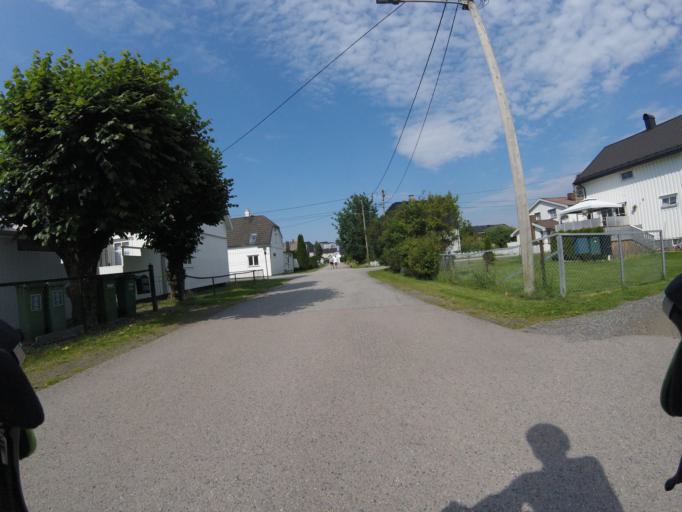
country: NO
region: Akershus
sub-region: Skedsmo
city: Lillestrom
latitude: 59.9563
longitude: 11.0631
